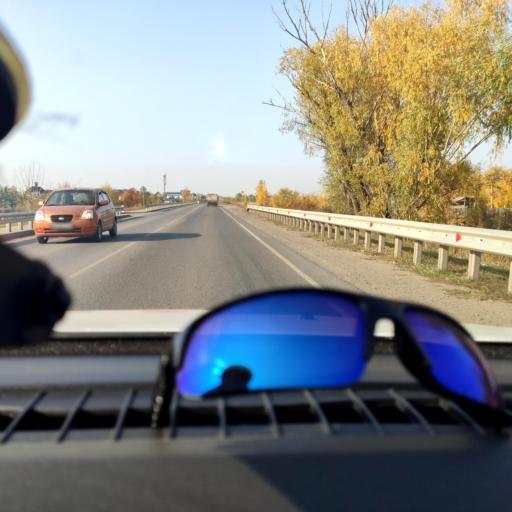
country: RU
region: Samara
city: Samara
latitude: 53.1193
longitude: 50.1207
